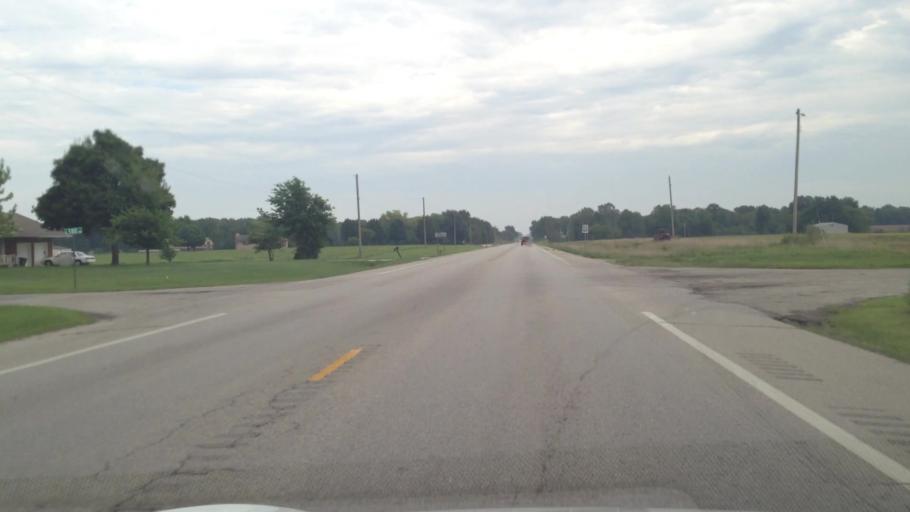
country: US
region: Kansas
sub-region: Crawford County
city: Pittsburg
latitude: 37.3391
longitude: -94.7783
